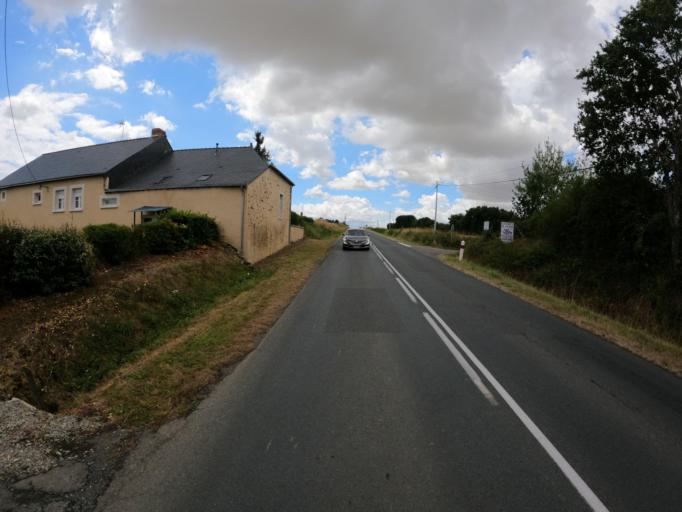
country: FR
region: Pays de la Loire
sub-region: Departement de Maine-et-Loire
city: Mire
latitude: 47.7856
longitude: -0.4529
